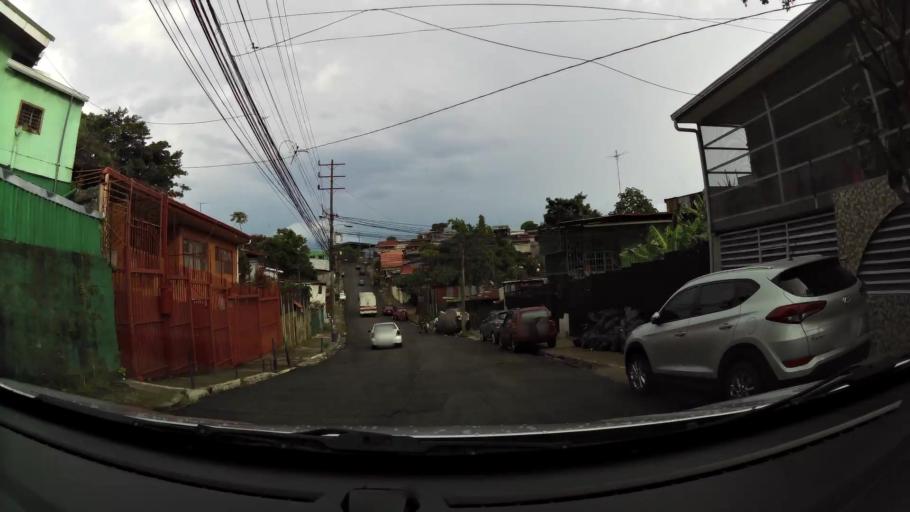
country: CR
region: San Jose
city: San Jose
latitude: 9.9395
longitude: -84.0929
